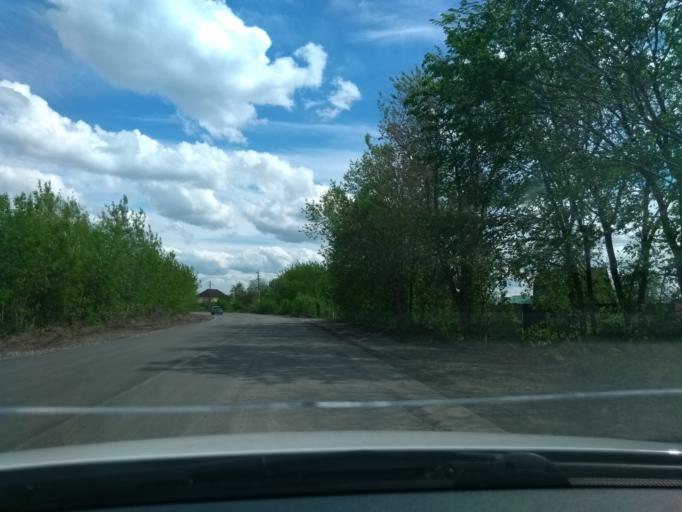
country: RU
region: Perm
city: Kondratovo
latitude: 58.0103
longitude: 56.0761
